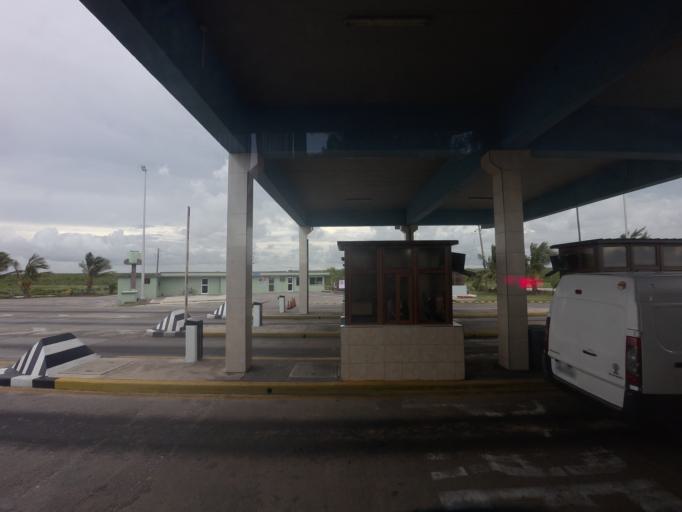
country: CU
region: Matanzas
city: Varadero
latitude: 23.1256
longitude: -81.3420
